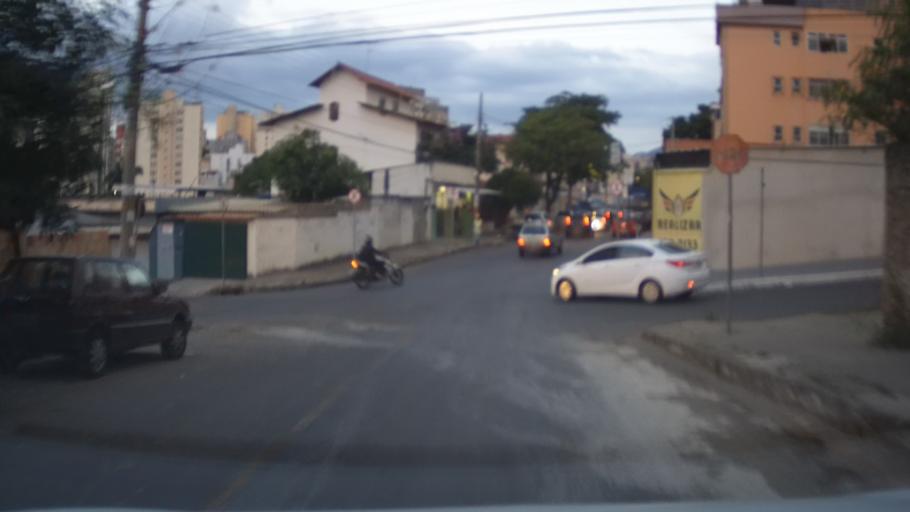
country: BR
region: Minas Gerais
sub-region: Belo Horizonte
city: Belo Horizonte
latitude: -19.8859
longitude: -43.9309
